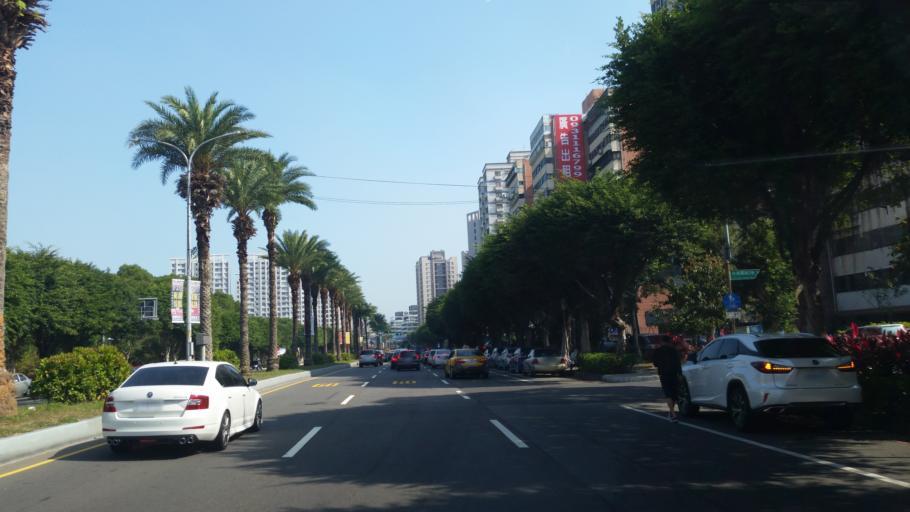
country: TW
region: Taiwan
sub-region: Taoyuan
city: Taoyuan
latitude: 25.0717
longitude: 121.3742
